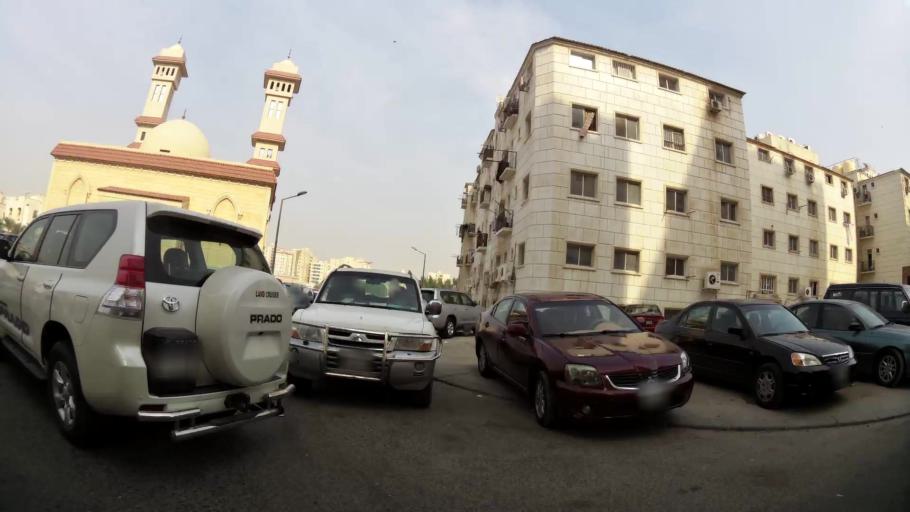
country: KW
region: Al Farwaniyah
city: Al Farwaniyah
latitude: 29.2821
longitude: 47.9517
